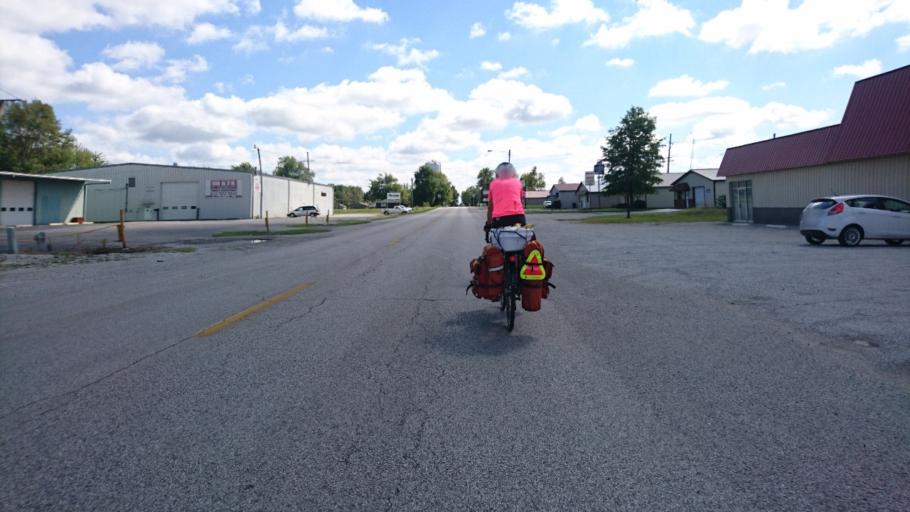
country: US
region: Illinois
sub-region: Montgomery County
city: Litchfield
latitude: 39.1765
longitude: -89.6667
